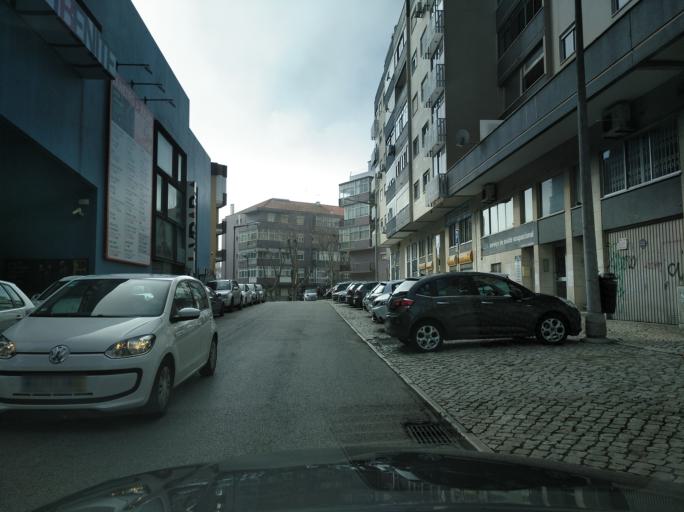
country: PT
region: Setubal
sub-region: Almada
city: Almada
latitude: 38.6766
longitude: -9.1599
